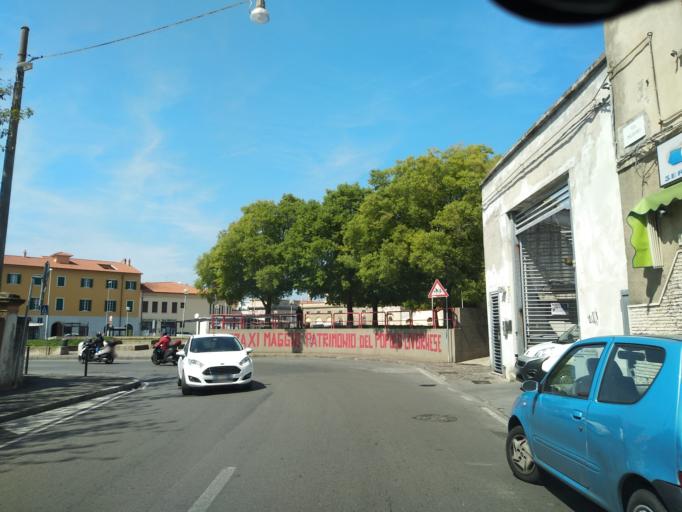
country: IT
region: Tuscany
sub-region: Provincia di Livorno
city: Livorno
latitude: 43.5593
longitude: 10.3154
